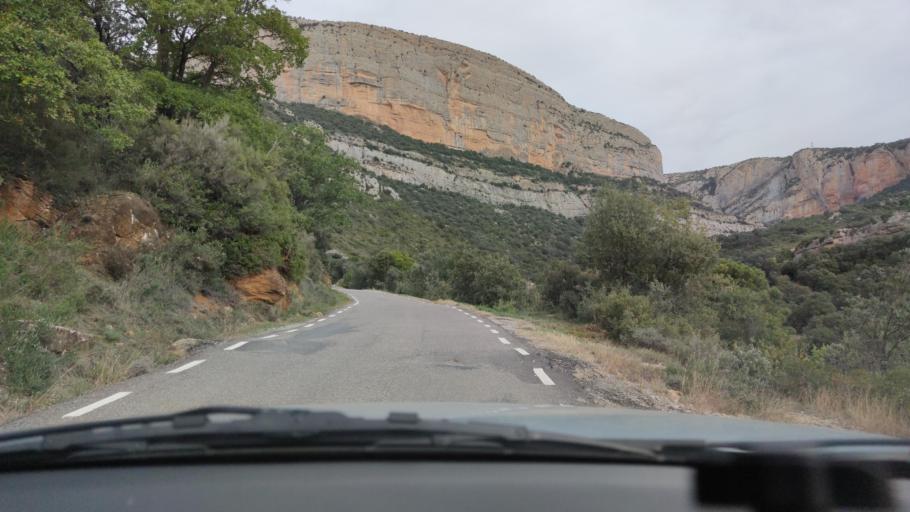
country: ES
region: Catalonia
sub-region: Provincia de Lleida
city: Artesa de Segre
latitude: 42.0146
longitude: 1.0294
